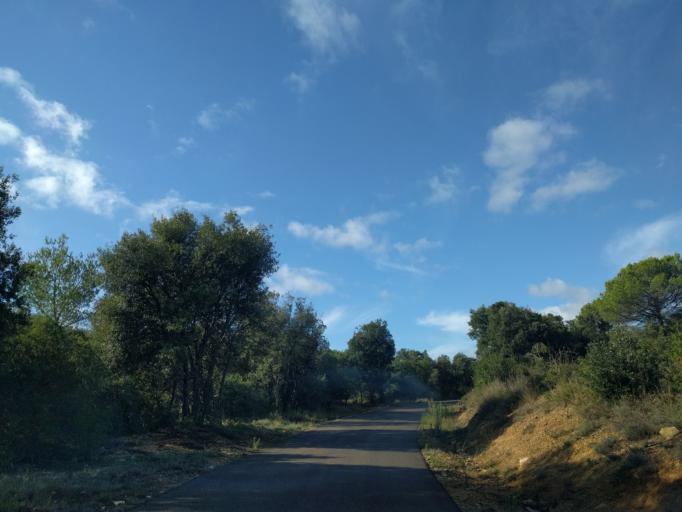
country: ES
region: Catalonia
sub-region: Provincia de Girona
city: la Cellera de Ter
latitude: 42.0164
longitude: 2.6347
